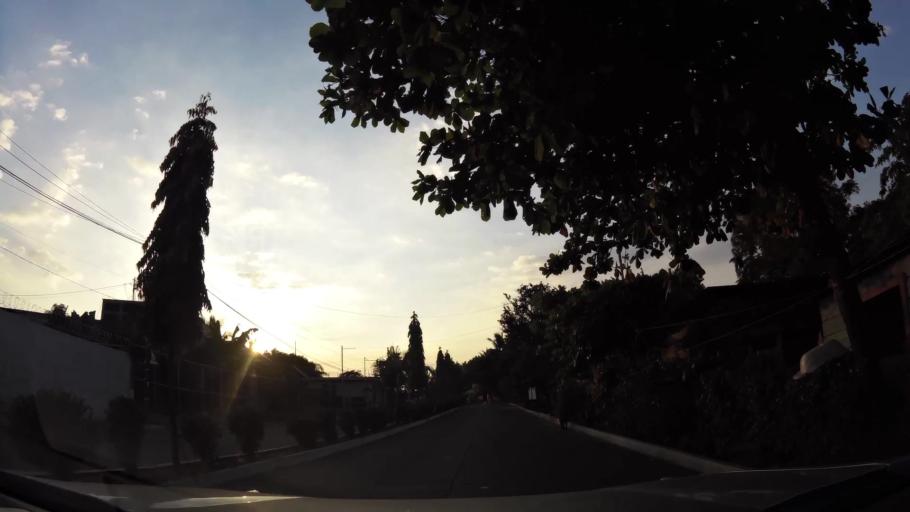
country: GT
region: Retalhuleu
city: San Sebastian
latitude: 14.5590
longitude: -91.6501
